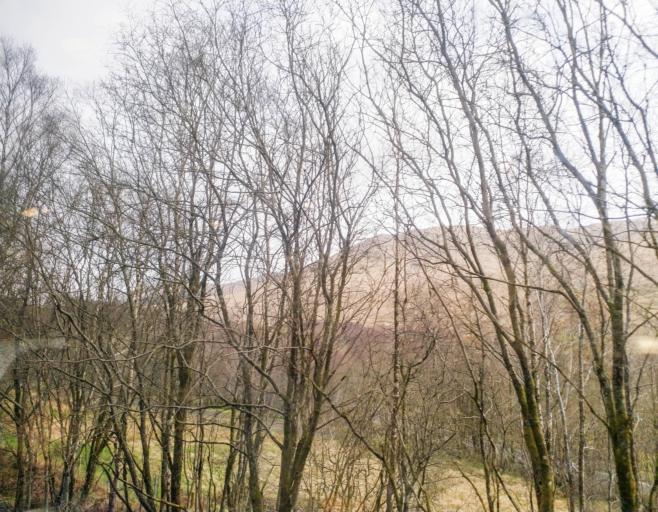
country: GB
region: Scotland
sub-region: Argyll and Bute
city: Garelochhead
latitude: 56.3604
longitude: -4.6773
